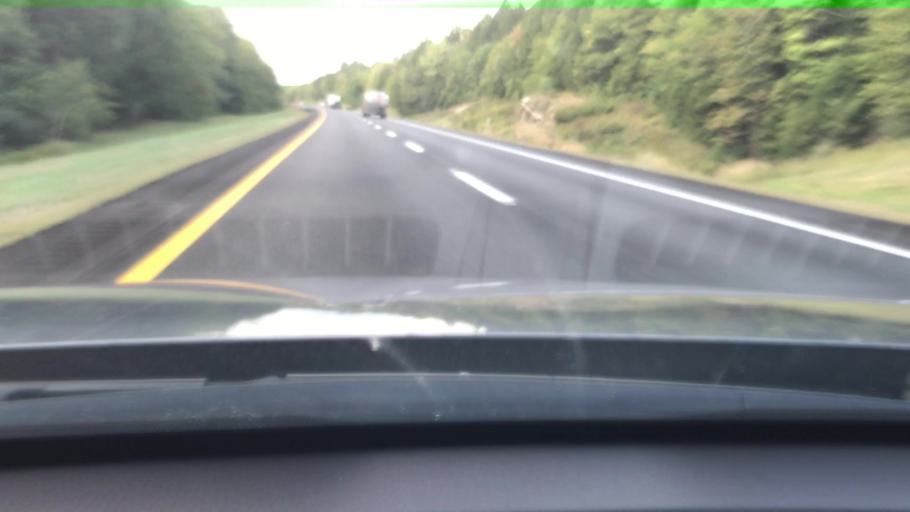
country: US
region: Maine
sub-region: Sagadahoc County
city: Richmond
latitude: 44.0548
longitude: -69.8905
